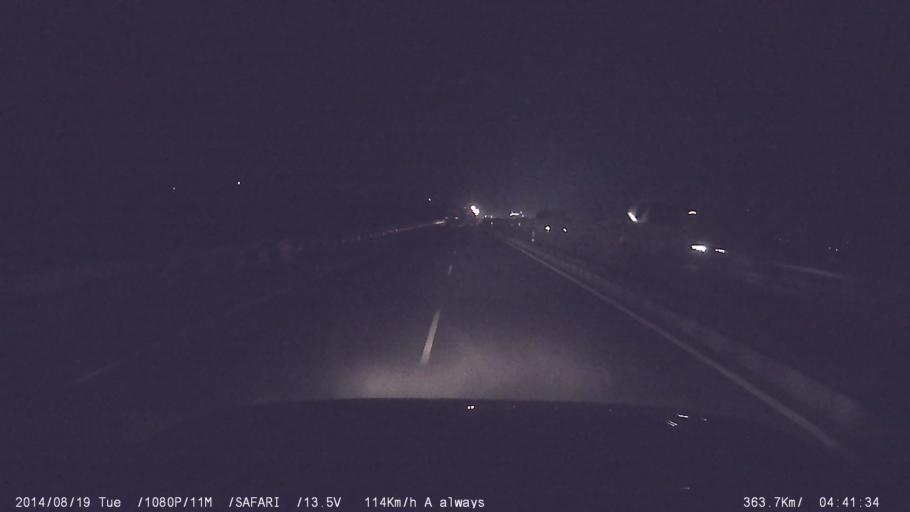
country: IN
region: Tamil Nadu
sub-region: Erode
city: Bhavani
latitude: 11.4056
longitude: 77.6584
